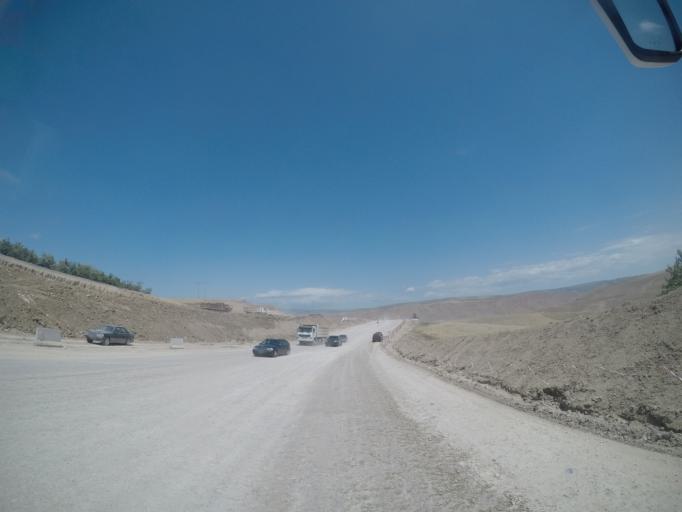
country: AZ
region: Qobustan
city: Qobustan
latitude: 40.5424
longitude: 48.7721
